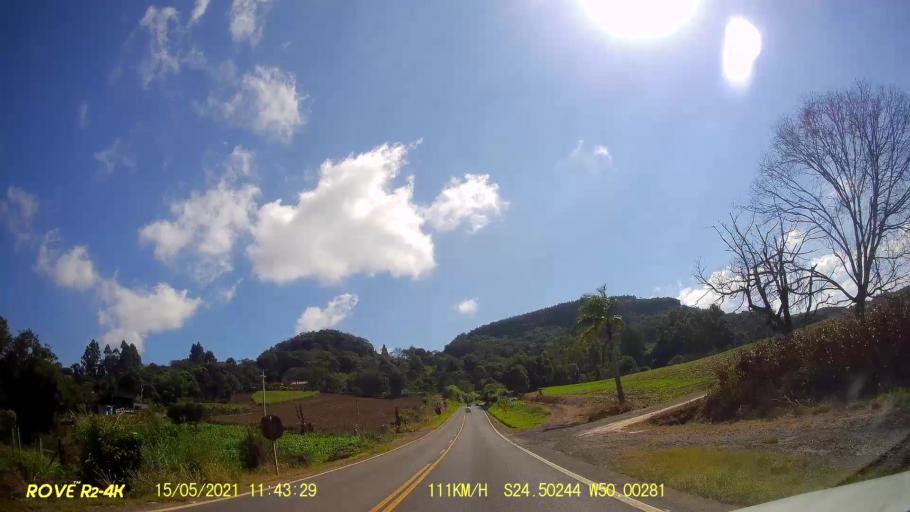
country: BR
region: Parana
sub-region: Pirai Do Sul
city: Pirai do Sul
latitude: -24.5025
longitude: -50.0027
